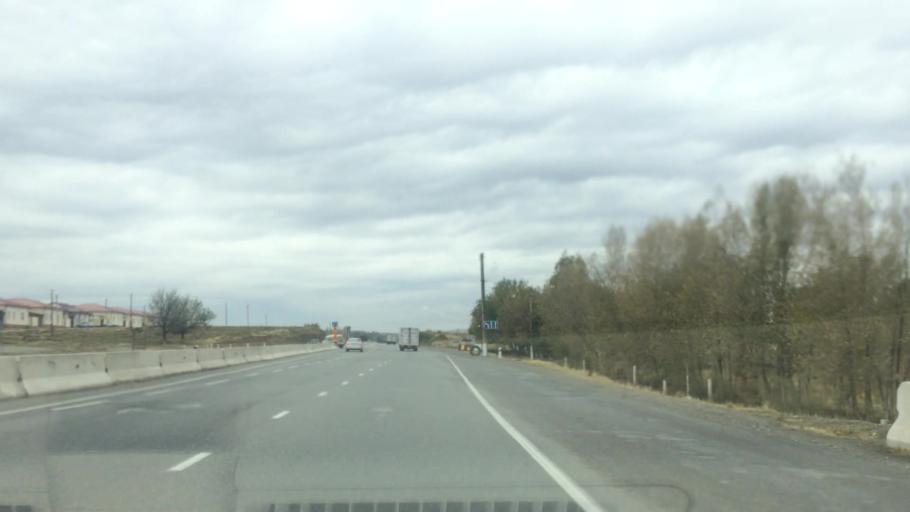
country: UZ
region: Jizzax
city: Jizzax
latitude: 39.9698
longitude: 67.5561
